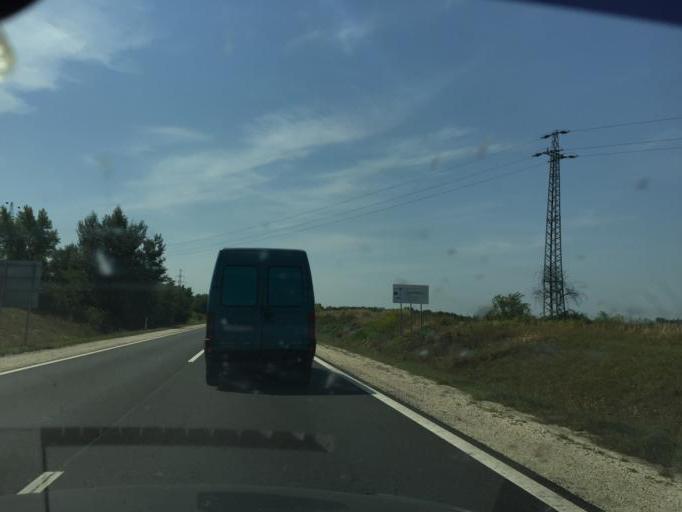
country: HU
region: Pest
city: Szod
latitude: 47.7548
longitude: 19.1794
